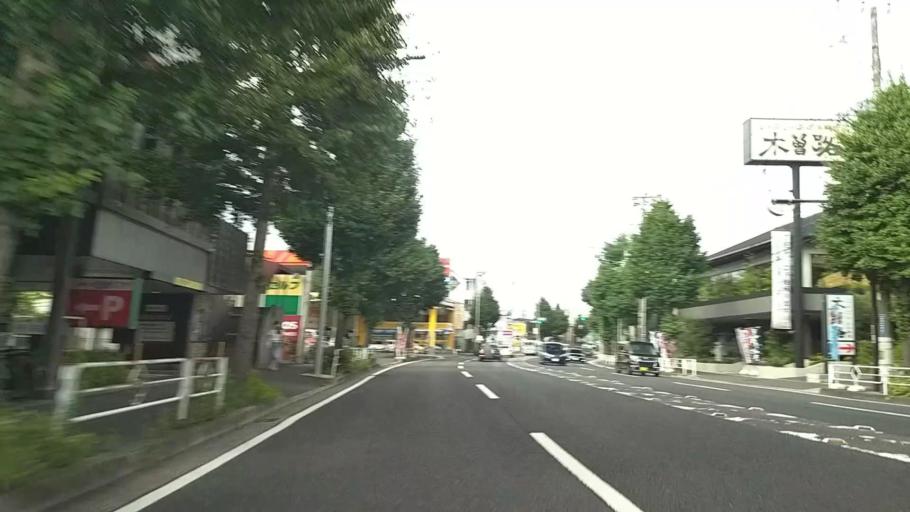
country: JP
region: Kanagawa
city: Yokohama
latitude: 35.3998
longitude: 139.5889
